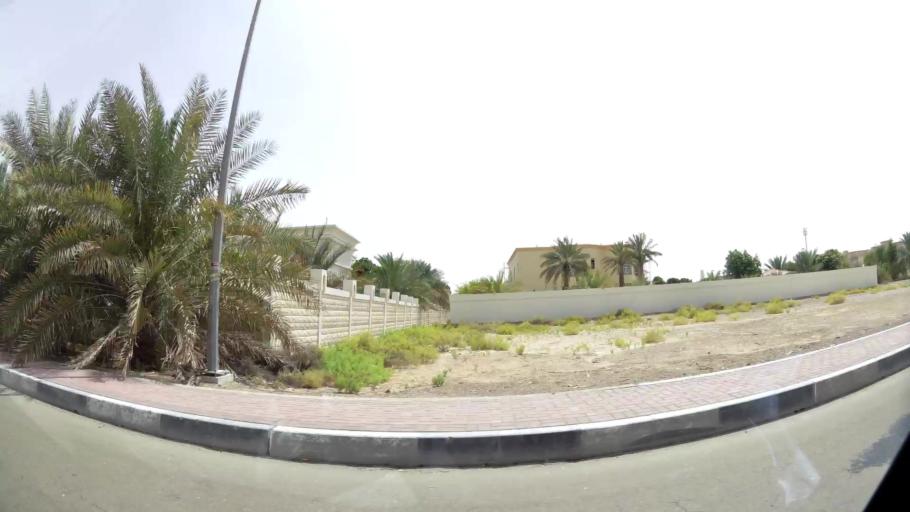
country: AE
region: Abu Dhabi
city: Al Ain
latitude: 24.1623
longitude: 55.6632
